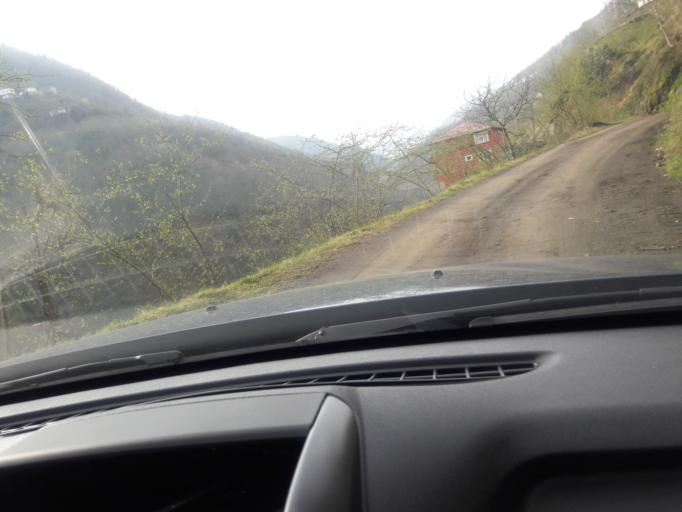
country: TR
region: Trabzon
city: Salpazari
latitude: 40.9708
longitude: 39.1967
